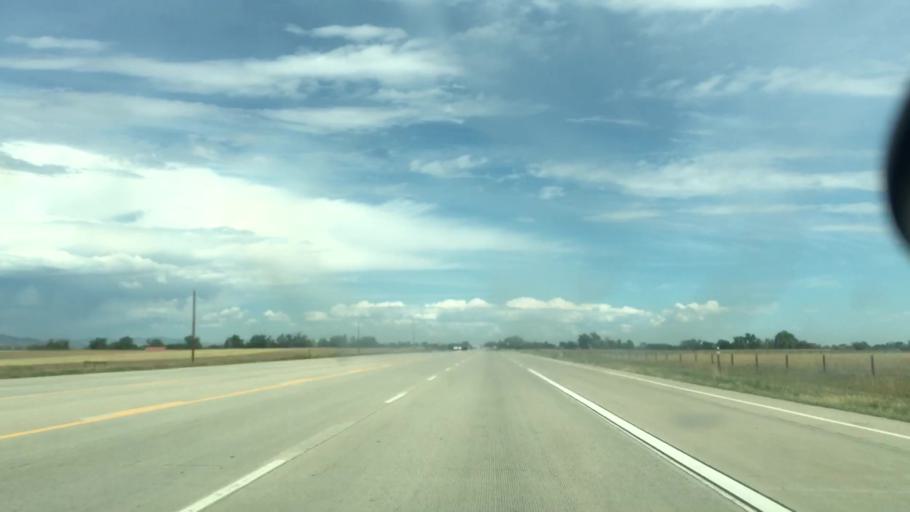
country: US
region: Colorado
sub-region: Boulder County
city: Longmont
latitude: 40.2194
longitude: -105.1023
